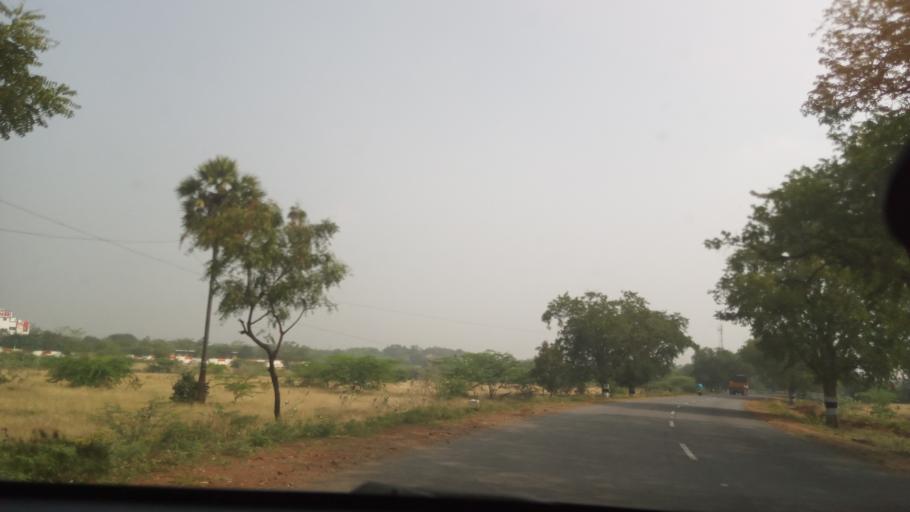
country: IN
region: Tamil Nadu
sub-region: Erode
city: Punjai Puliyampatti
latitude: 11.4282
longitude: 77.1973
